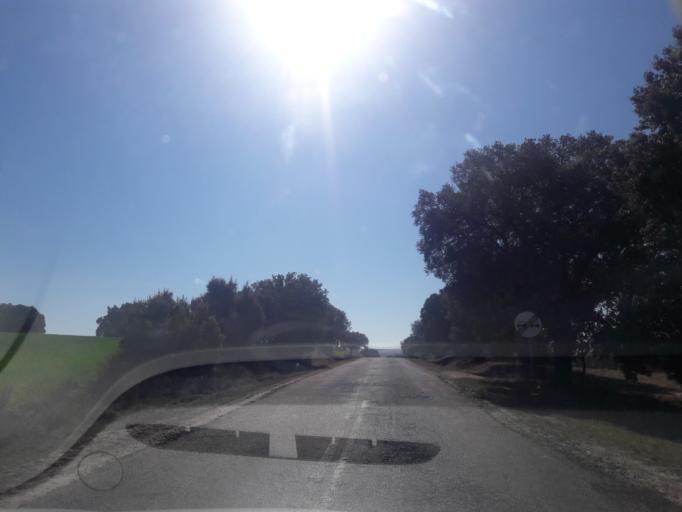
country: ES
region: Castille and Leon
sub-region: Provincia de Avila
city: Mancera de Arriba
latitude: 40.8151
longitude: -5.1666
